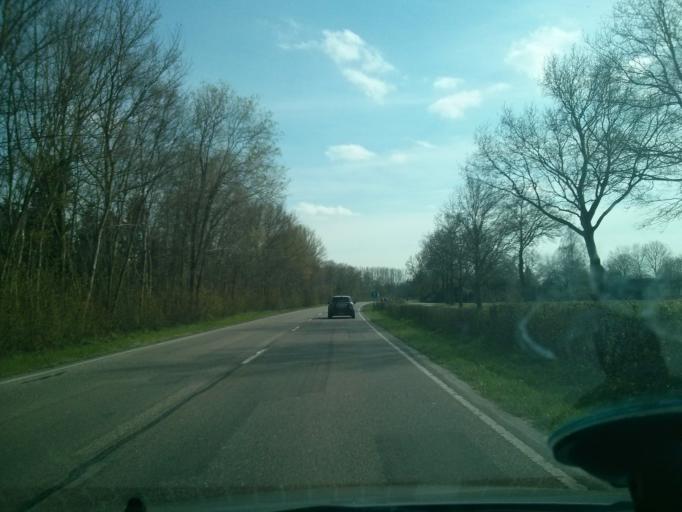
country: NL
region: North Brabant
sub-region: Gemeente Son en Breugel
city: Son
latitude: 51.4971
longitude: 5.4963
